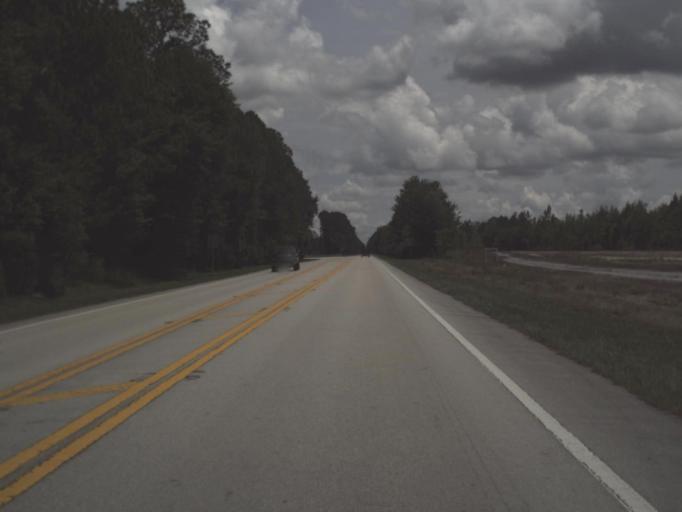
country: US
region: Florida
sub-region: Nassau County
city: Yulee
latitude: 30.7026
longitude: -81.6650
